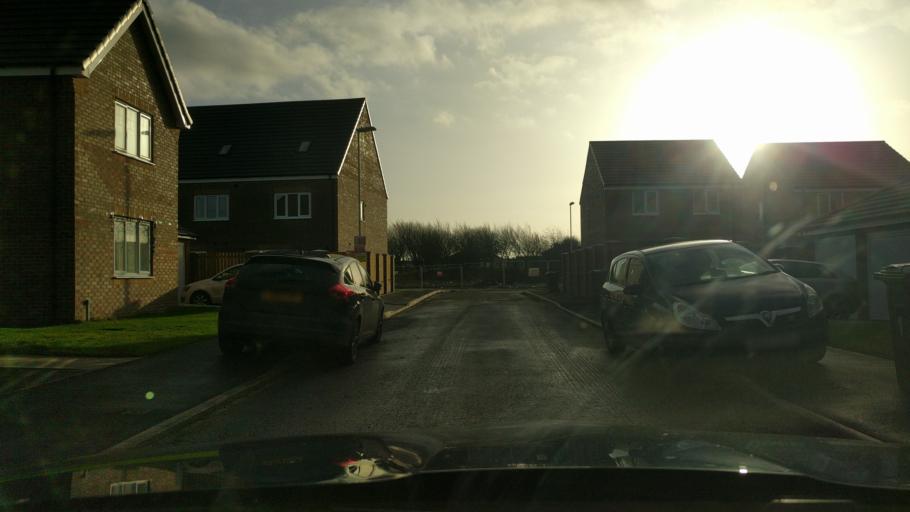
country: GB
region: England
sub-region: Northumberland
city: Ashington
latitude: 55.1862
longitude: -1.5915
